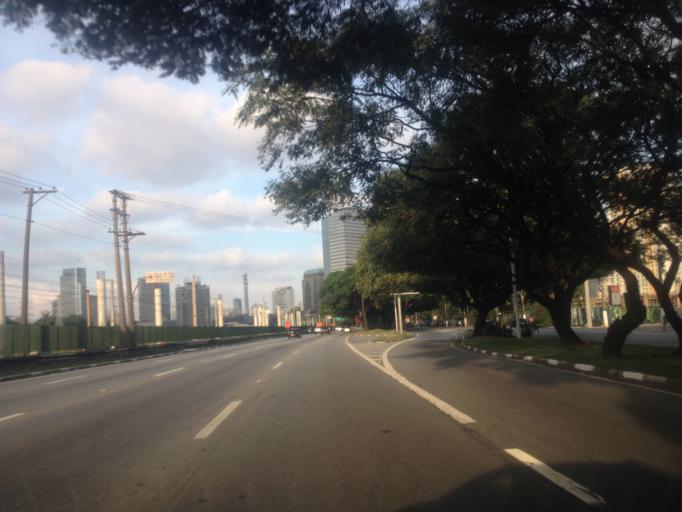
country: BR
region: Sao Paulo
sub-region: Taboao Da Serra
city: Taboao da Serra
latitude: -23.6253
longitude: -46.7084
